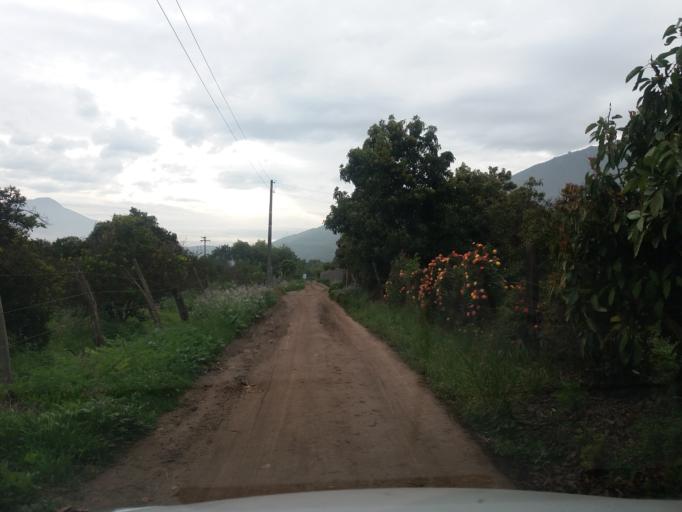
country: CL
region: Valparaiso
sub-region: Provincia de San Felipe
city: Llaillay
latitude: -32.8481
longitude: -71.0595
